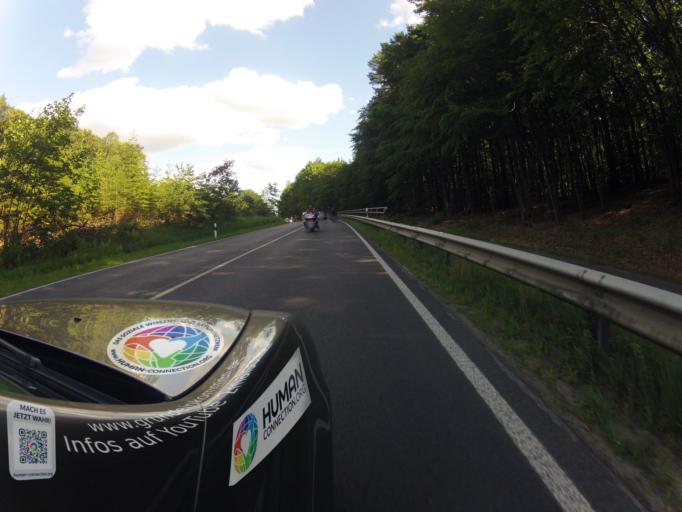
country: DE
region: Mecklenburg-Vorpommern
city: Seebad Bansin
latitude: 53.9703
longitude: 14.1186
